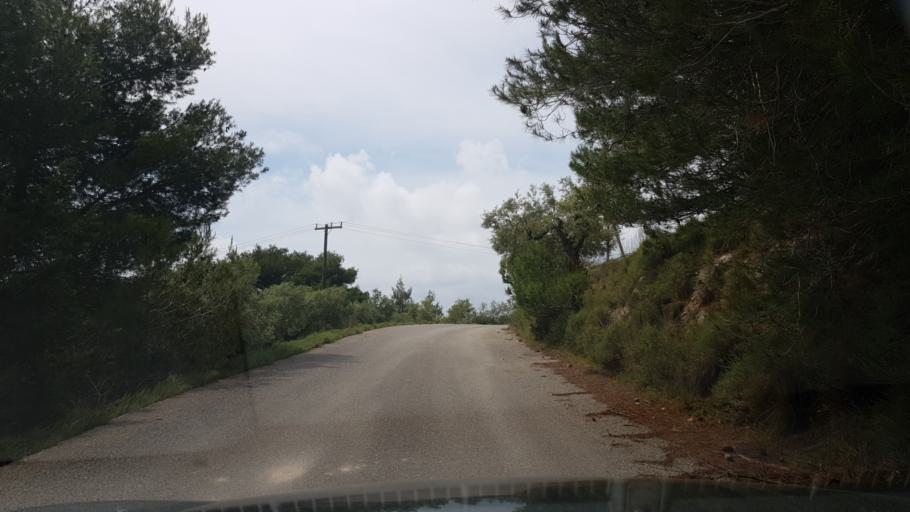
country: GR
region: Ionian Islands
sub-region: Lefkada
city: Nidri
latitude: 38.6264
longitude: 20.5646
